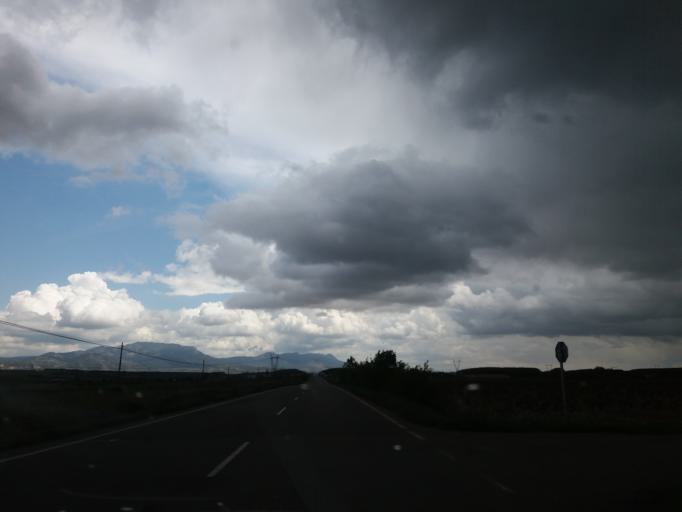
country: ES
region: La Rioja
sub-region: Provincia de La Rioja
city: Cihuri
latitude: 42.5738
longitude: -2.9279
